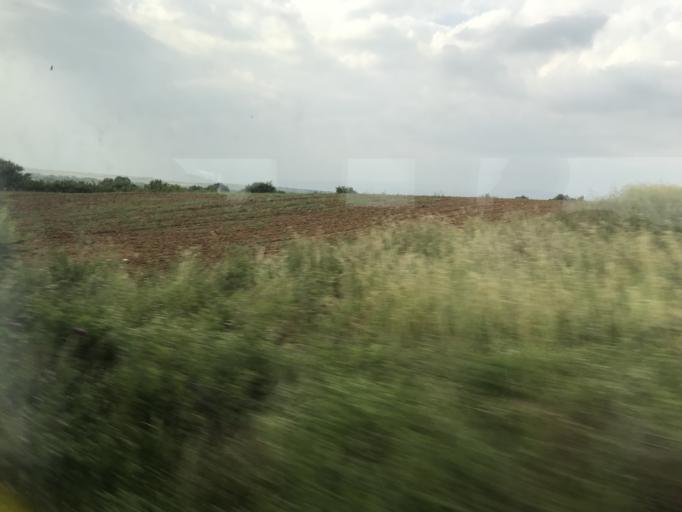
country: GR
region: East Macedonia and Thrace
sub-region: Nomos Rodopis
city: Sapes
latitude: 41.0332
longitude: 25.6764
